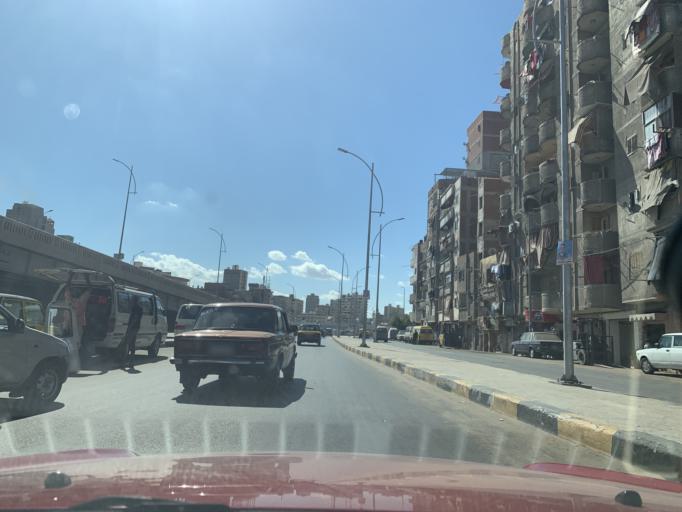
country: EG
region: Alexandria
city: Alexandria
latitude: 31.2248
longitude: 29.9782
